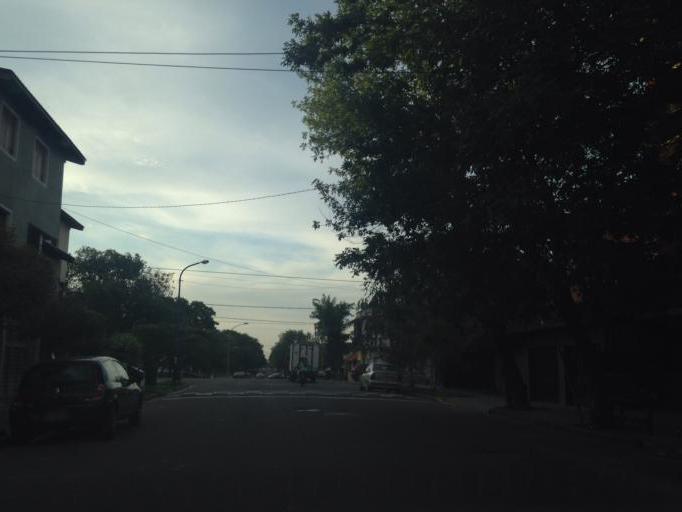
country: AR
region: Buenos Aires
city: Mar del Plata
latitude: -38.0155
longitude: -57.5506
